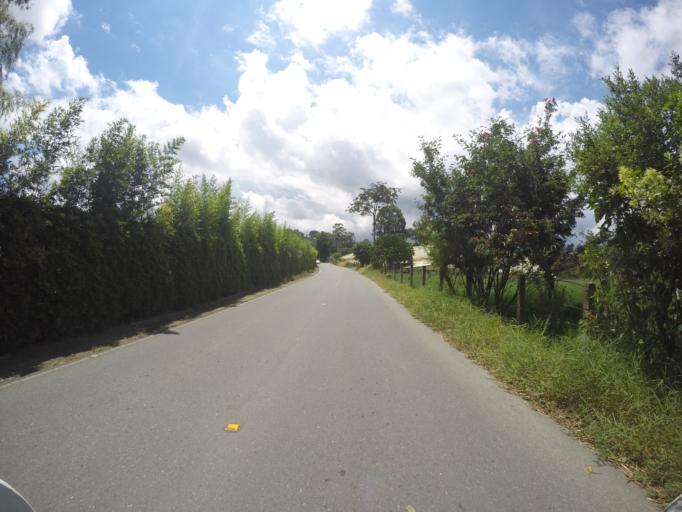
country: CO
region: Quindio
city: Filandia
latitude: 4.6404
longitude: -75.6854
